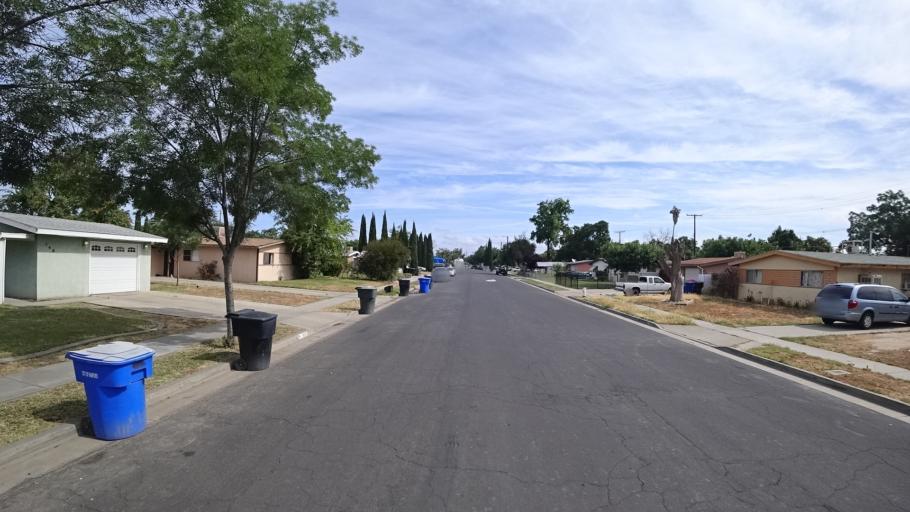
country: US
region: California
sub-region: Kings County
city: Hanford
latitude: 36.3146
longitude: -119.6660
